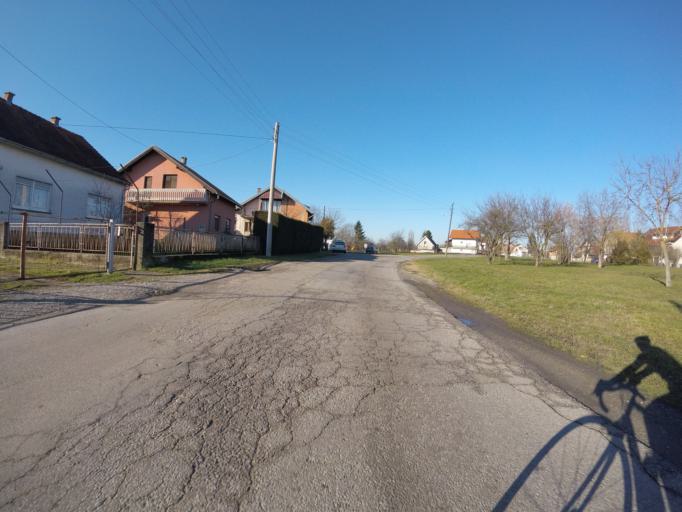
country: HR
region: Zagrebacka
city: Gradici
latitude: 45.7009
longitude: 16.0601
